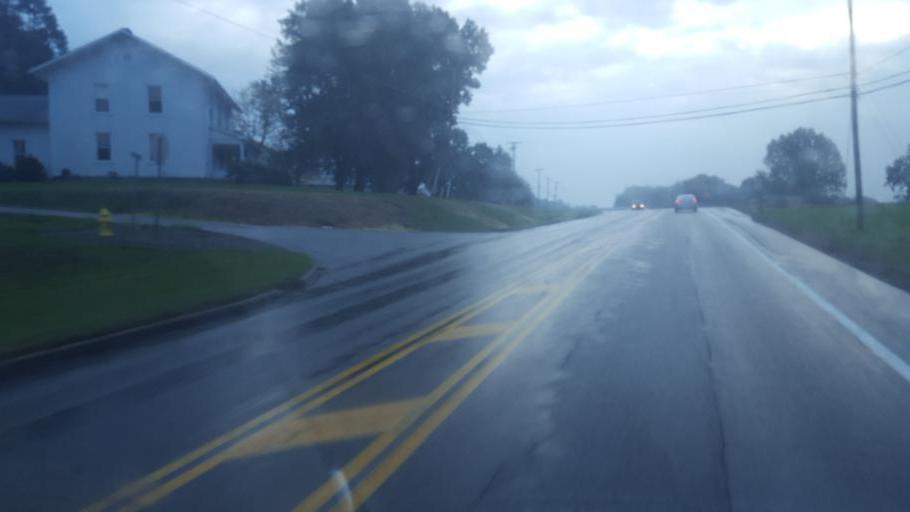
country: US
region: Ohio
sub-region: Wayne County
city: Wooster
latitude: 40.7728
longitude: -81.9200
